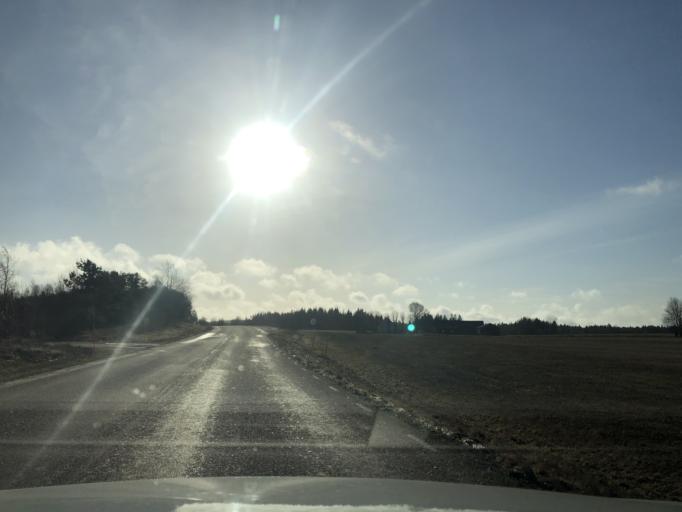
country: SE
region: Vaestra Goetaland
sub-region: Ulricehamns Kommun
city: Ulricehamn
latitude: 57.8159
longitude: 13.5336
